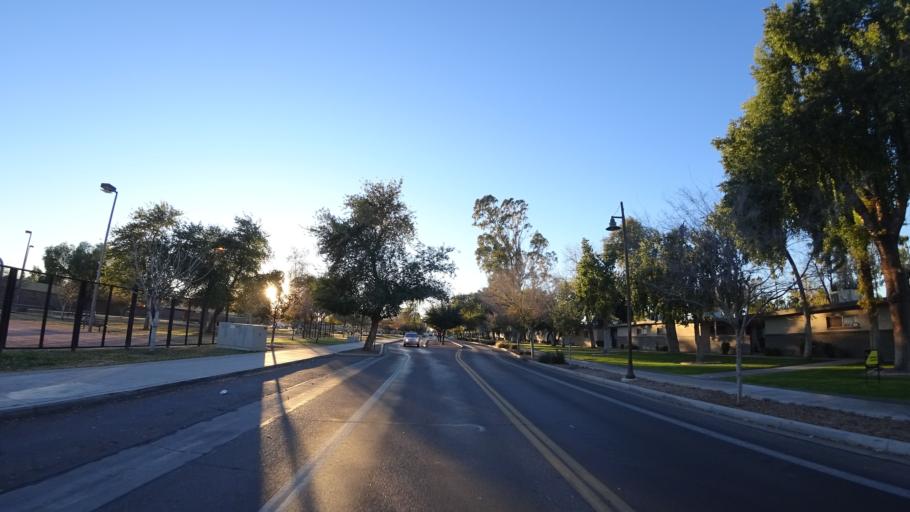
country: US
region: Arizona
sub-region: Maricopa County
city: Tempe Junction
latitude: 33.4255
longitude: -111.9507
